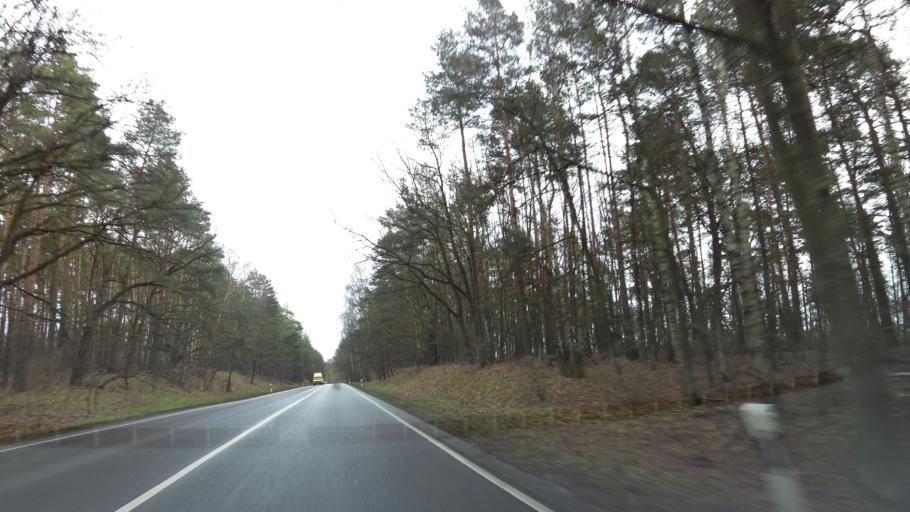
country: DE
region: Brandenburg
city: Strausberg
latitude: 52.5917
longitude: 13.8808
